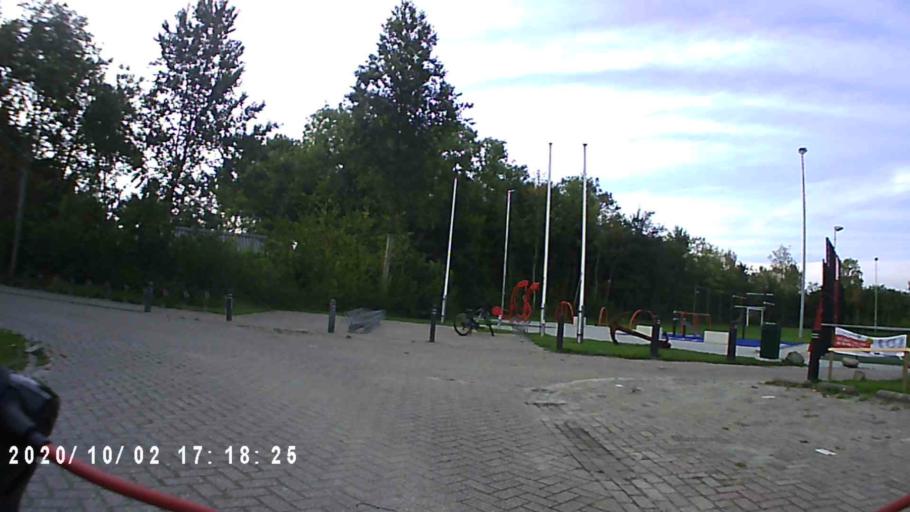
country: NL
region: Groningen
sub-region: Gemeente De Marne
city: Ulrum
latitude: 53.3403
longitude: 6.3065
